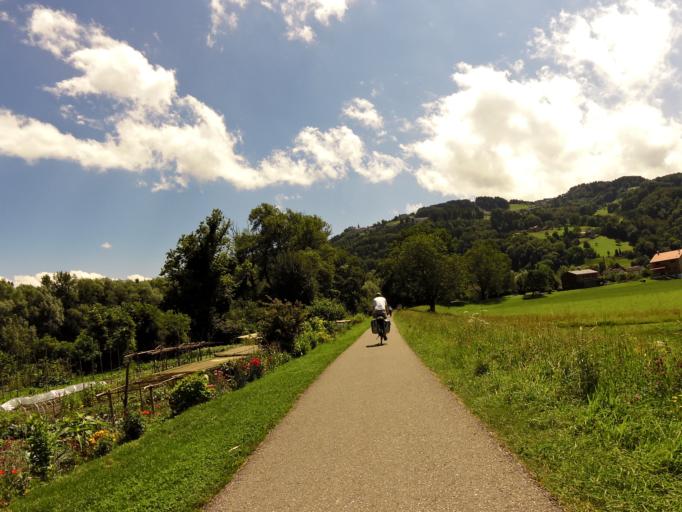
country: AT
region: Vorarlberg
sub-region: Politischer Bezirk Bregenz
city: Gaissau
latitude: 47.4659
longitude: 9.6045
